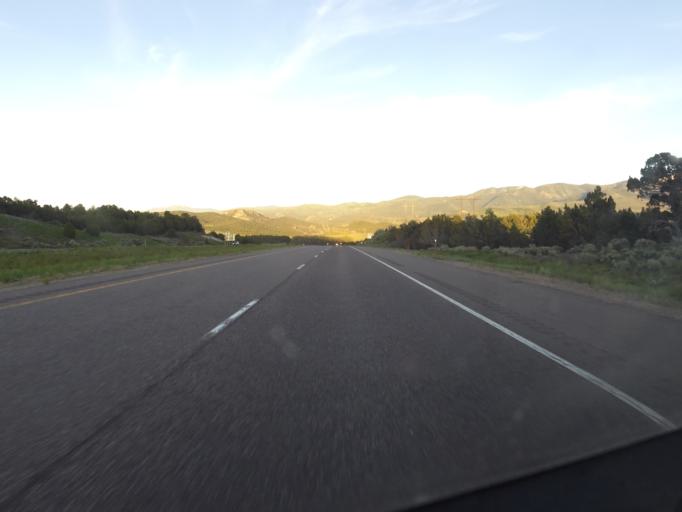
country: US
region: Utah
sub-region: Beaver County
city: Beaver
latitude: 38.5776
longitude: -112.4758
